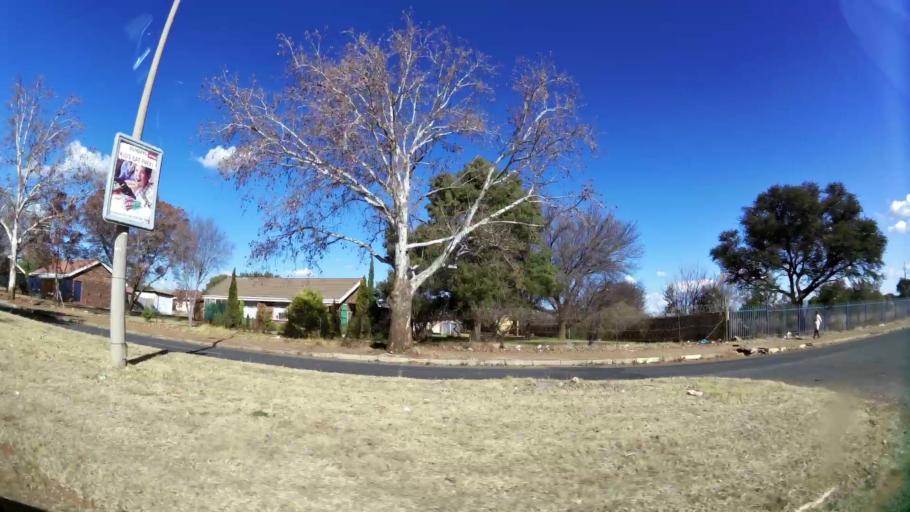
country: ZA
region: Gauteng
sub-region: West Rand District Municipality
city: Carletonville
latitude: -26.3583
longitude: 27.3862
